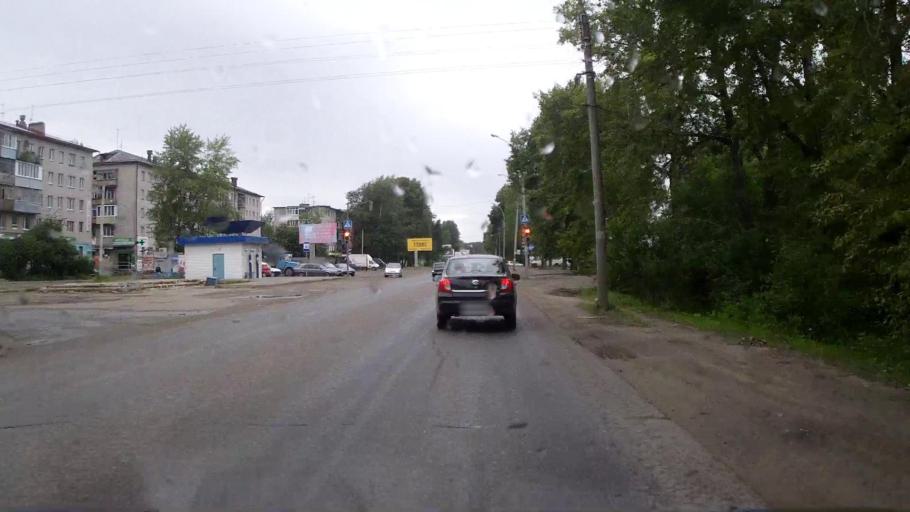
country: RU
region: Vologda
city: Vologda
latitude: 59.2056
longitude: 39.8641
